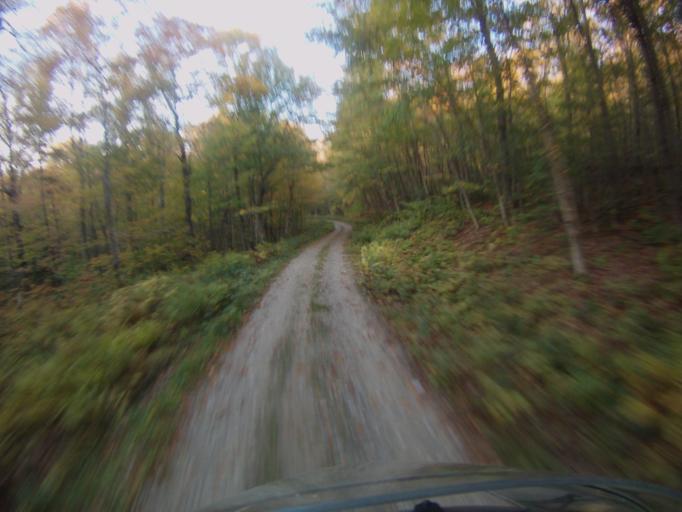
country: US
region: Vermont
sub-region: Addison County
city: Bristol
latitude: 44.0822
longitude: -72.9393
